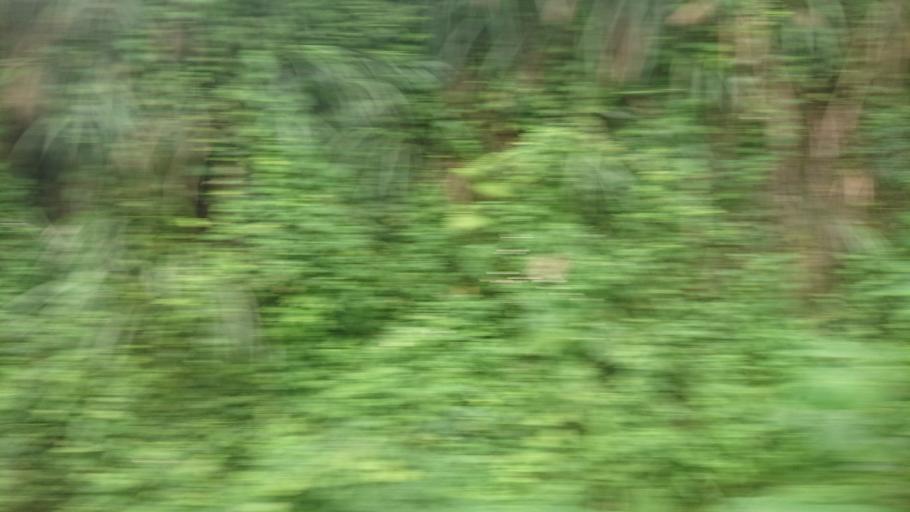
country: TW
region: Taiwan
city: Lugu
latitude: 23.8230
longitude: 120.8349
